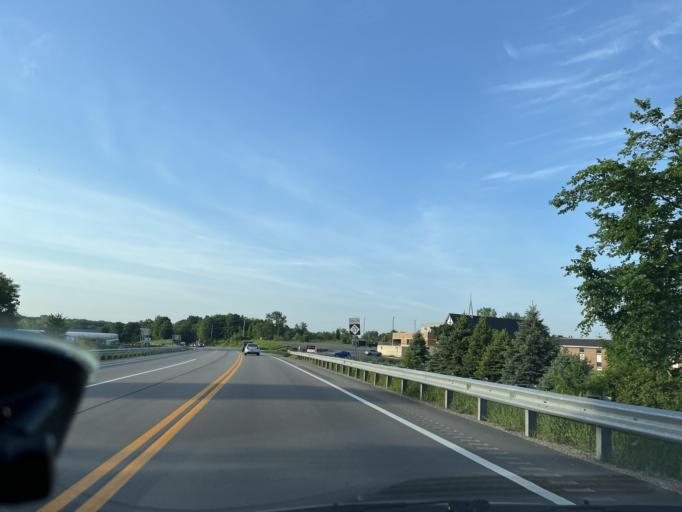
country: US
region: Michigan
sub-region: Kent County
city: Caledonia
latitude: 42.7542
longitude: -85.5050
